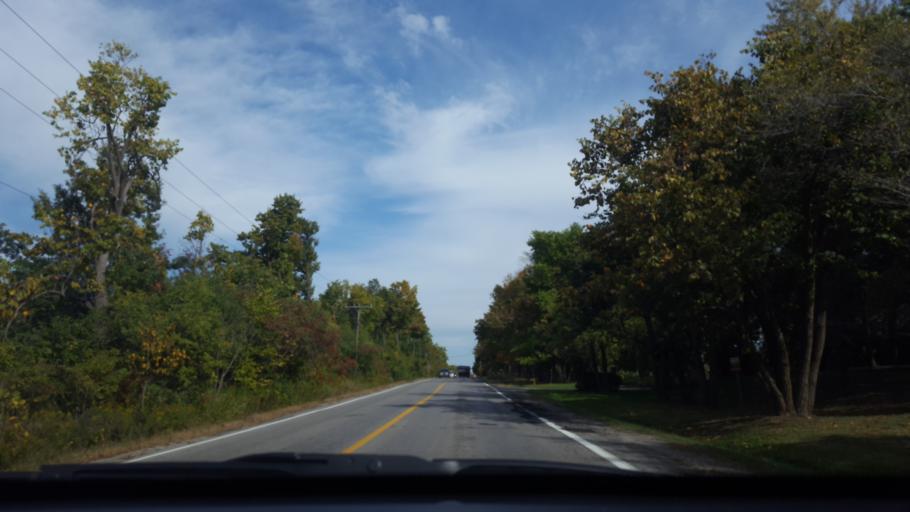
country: CA
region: Ontario
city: Vaughan
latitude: 43.8615
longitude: -79.5738
